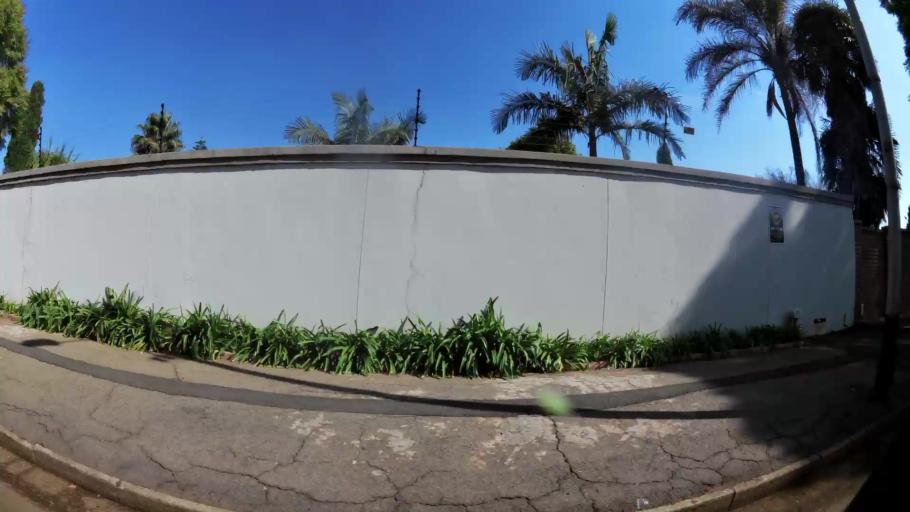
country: ZA
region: Gauteng
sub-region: City of Johannesburg Metropolitan Municipality
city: Johannesburg
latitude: -26.1599
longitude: 28.0134
